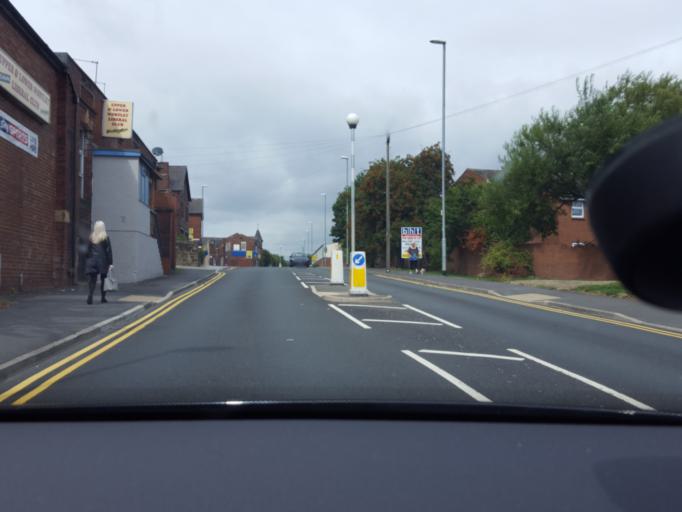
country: GB
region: England
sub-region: City and Borough of Leeds
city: Leeds
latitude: 53.7915
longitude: -1.5932
